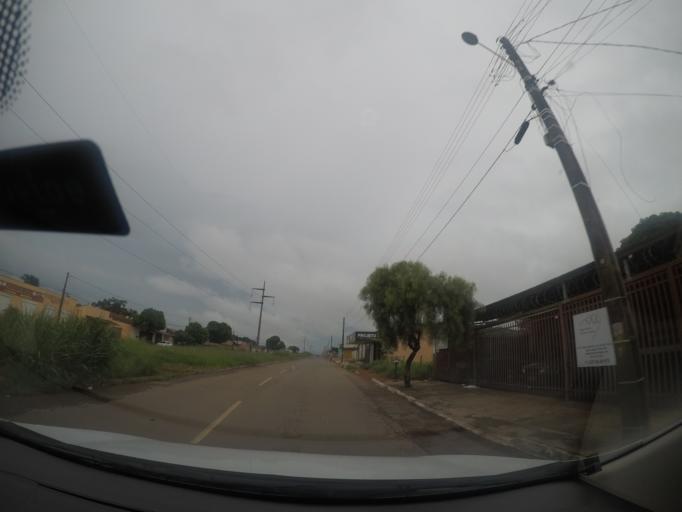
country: BR
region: Goias
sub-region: Aparecida De Goiania
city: Aparecida de Goiania
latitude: -16.7714
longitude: -49.2978
